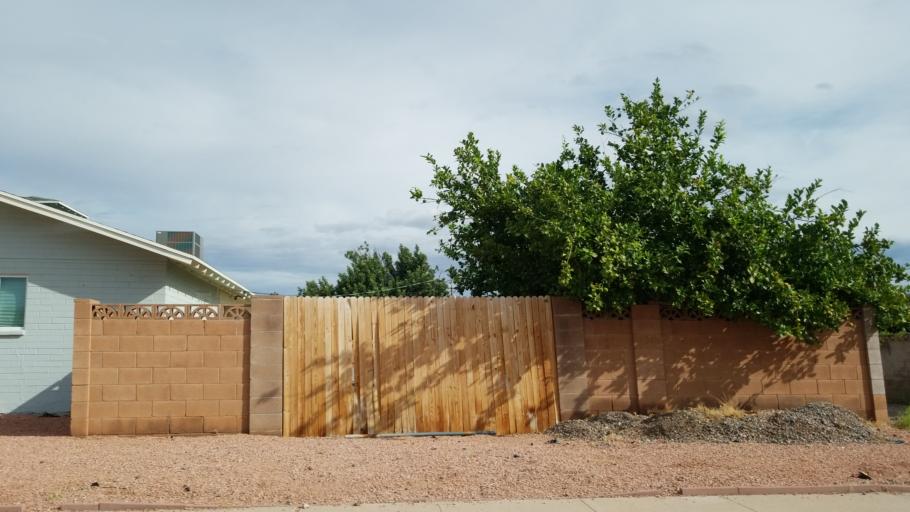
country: US
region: Arizona
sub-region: Maricopa County
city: Scottsdale
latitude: 33.4731
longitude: -111.9045
